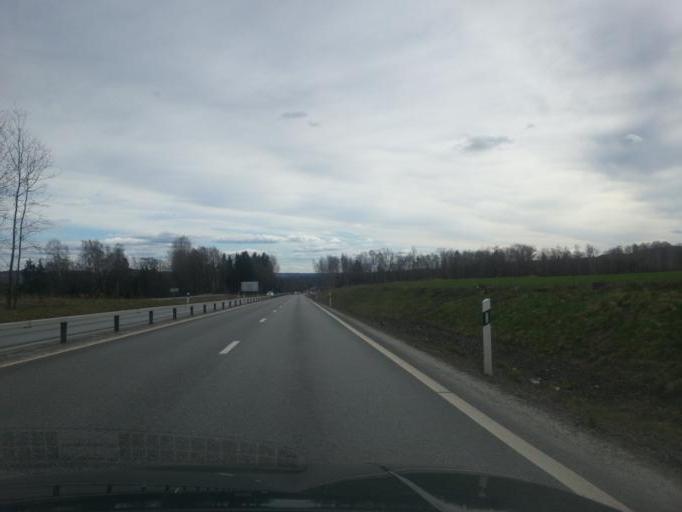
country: SE
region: Joenkoeping
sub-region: Habo Kommun
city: Habo
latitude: 57.8981
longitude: 14.1056
